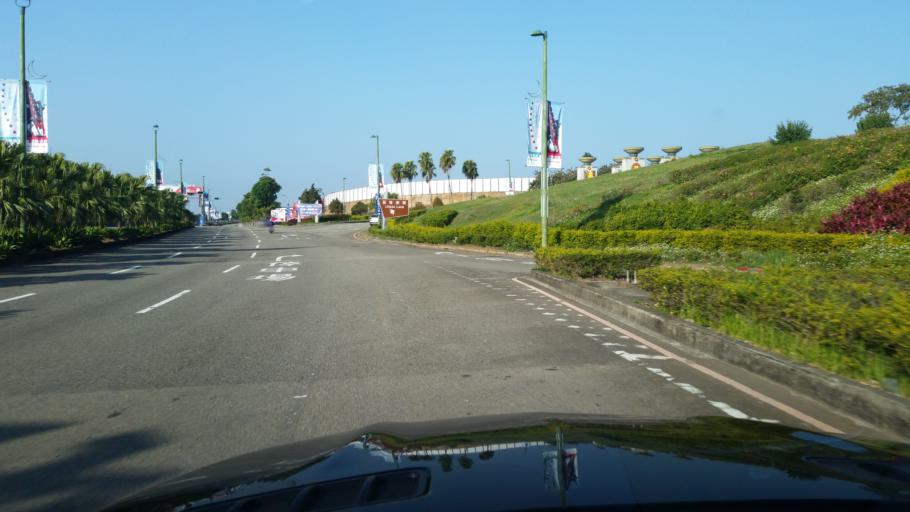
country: TW
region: Taiwan
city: Fengyuan
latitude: 24.3181
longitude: 120.6933
